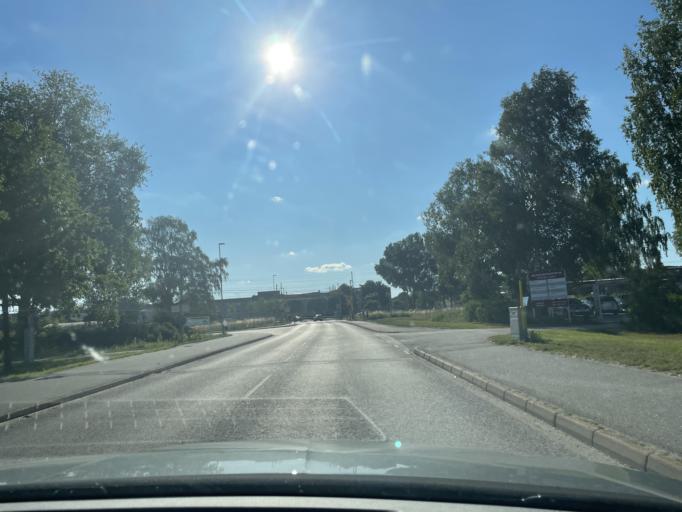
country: SE
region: Stockholm
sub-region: Sigtuna Kommun
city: Marsta
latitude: 59.6304
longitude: 17.8632
